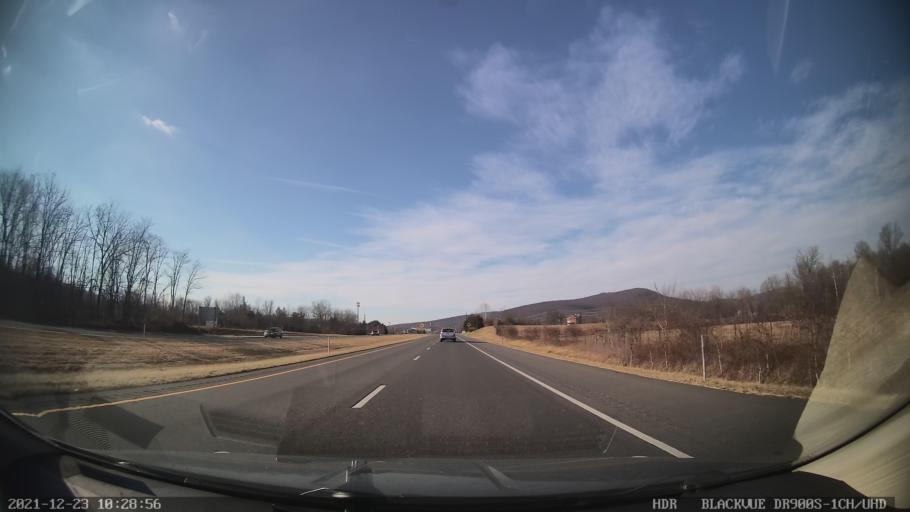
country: US
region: Maryland
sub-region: Frederick County
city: Emmitsburg
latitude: 39.6891
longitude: -77.3291
